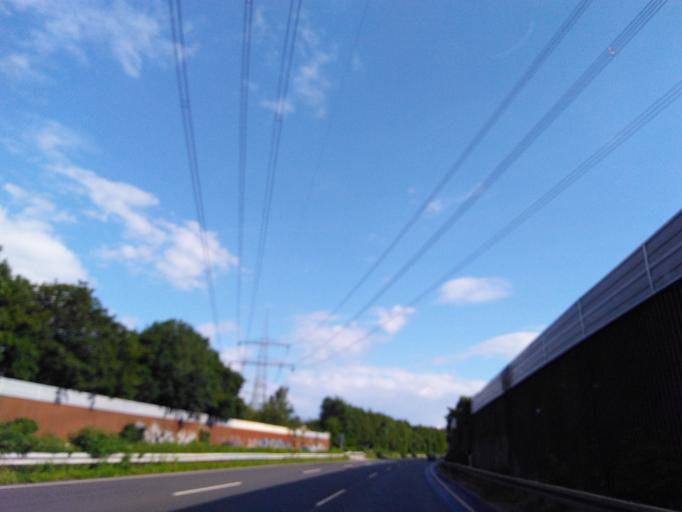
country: DE
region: North Rhine-Westphalia
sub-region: Regierungsbezirk Arnsberg
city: Dortmund
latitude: 51.4629
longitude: 7.4831
